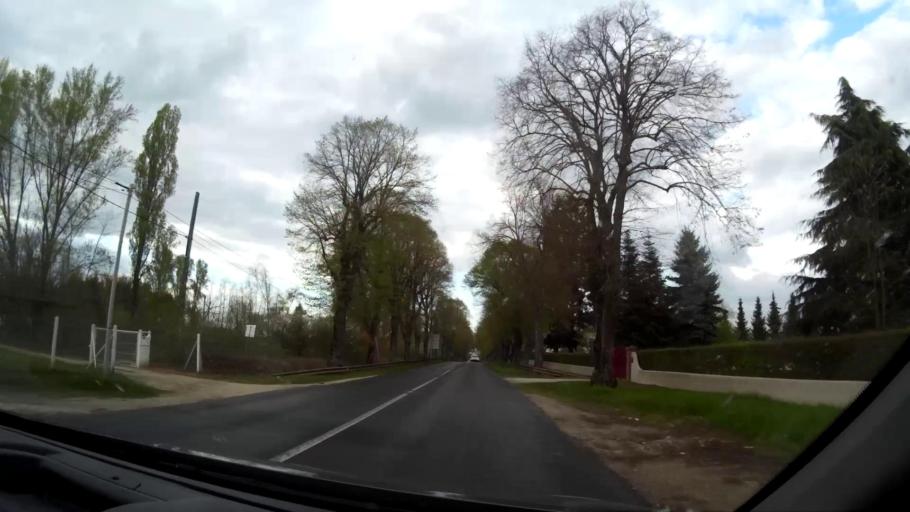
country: FR
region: Centre
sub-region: Departement du Loir-et-Cher
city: Contres
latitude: 47.4301
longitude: 1.4279
